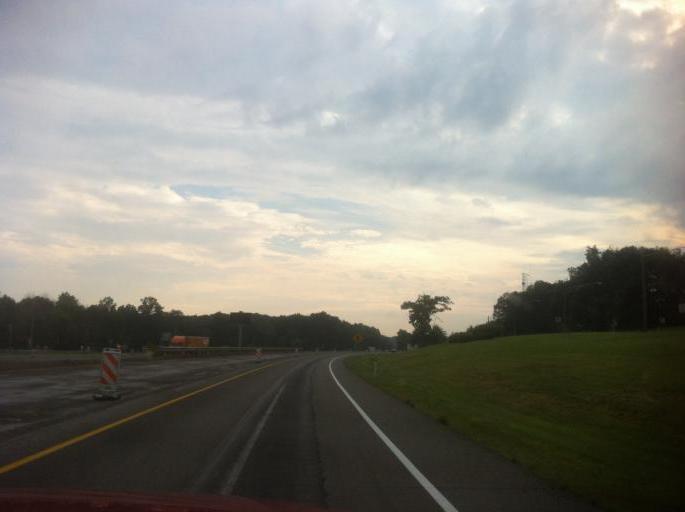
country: US
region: Pennsylvania
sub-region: Clarion County
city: Knox
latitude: 41.1974
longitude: -79.4996
